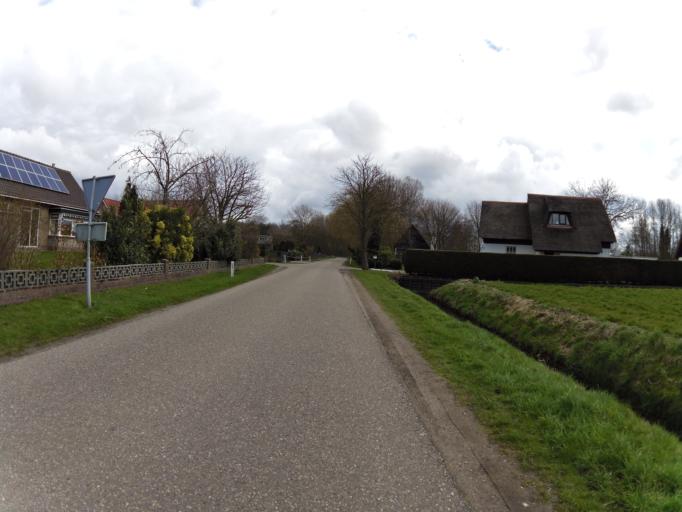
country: NL
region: South Holland
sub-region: Gemeente Hellevoetsluis
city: Nieuwenhoorn
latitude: 51.8986
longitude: 4.0934
